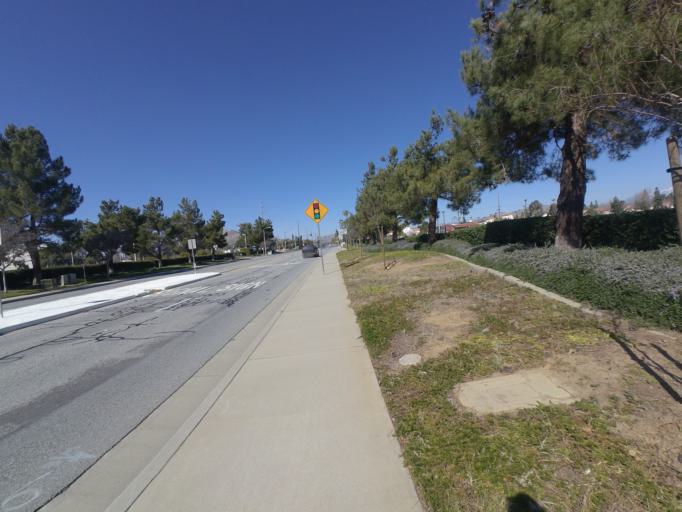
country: US
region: California
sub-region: Riverside County
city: March Air Force Base
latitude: 33.9156
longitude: -117.2611
